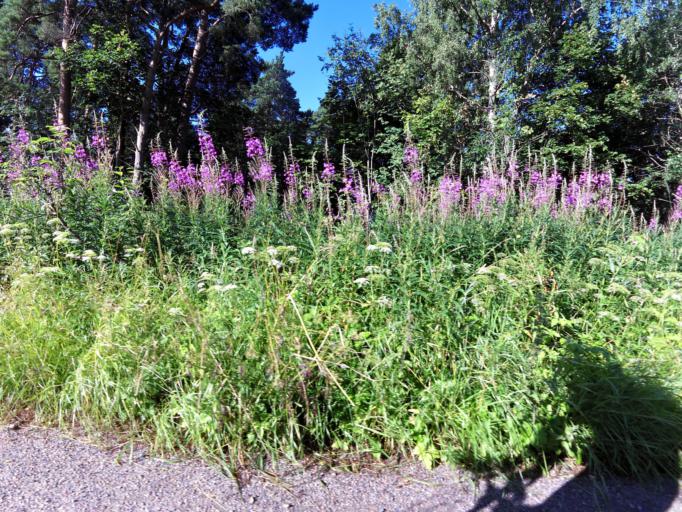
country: FI
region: Uusimaa
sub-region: Helsinki
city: Kauniainen
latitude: 60.1552
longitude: 24.7016
